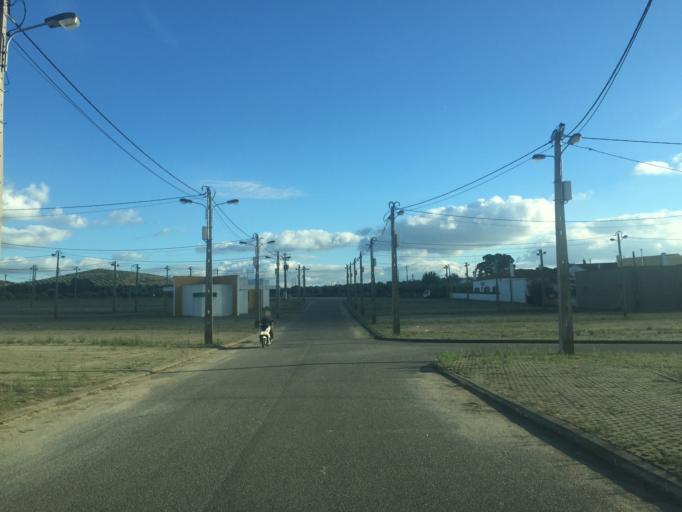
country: PT
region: Portalegre
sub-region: Alter do Chao
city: Alter do Chao
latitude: 39.1954
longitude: -7.6551
